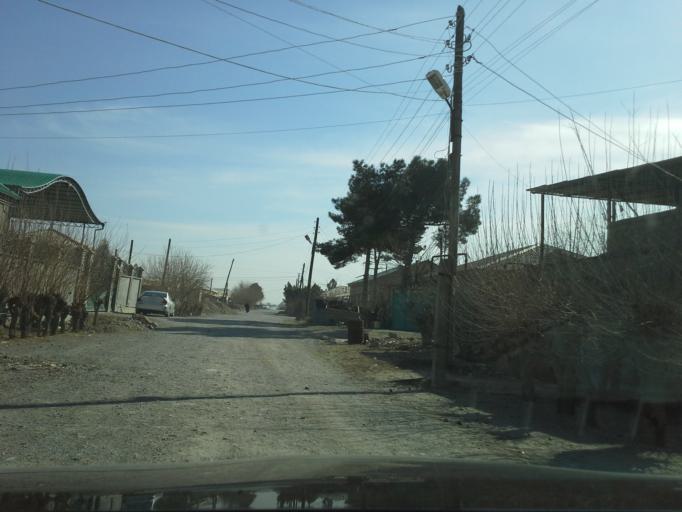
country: TM
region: Ahal
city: Abadan
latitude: 38.1278
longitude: 58.0020
